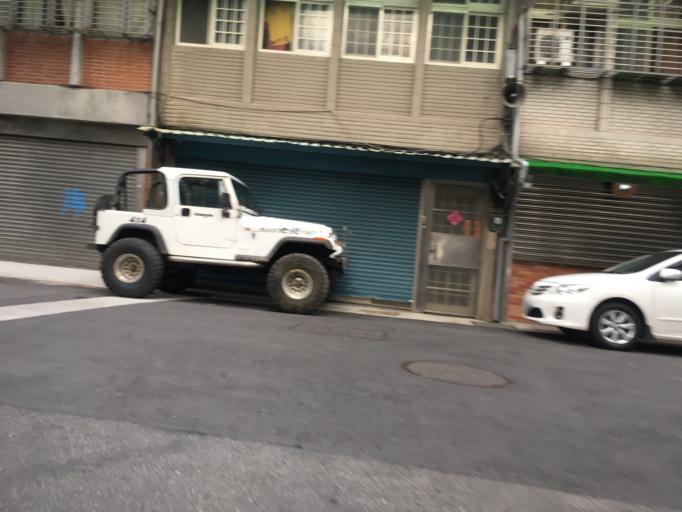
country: TW
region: Taiwan
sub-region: Taoyuan
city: Taoyuan
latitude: 24.9298
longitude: 121.3686
